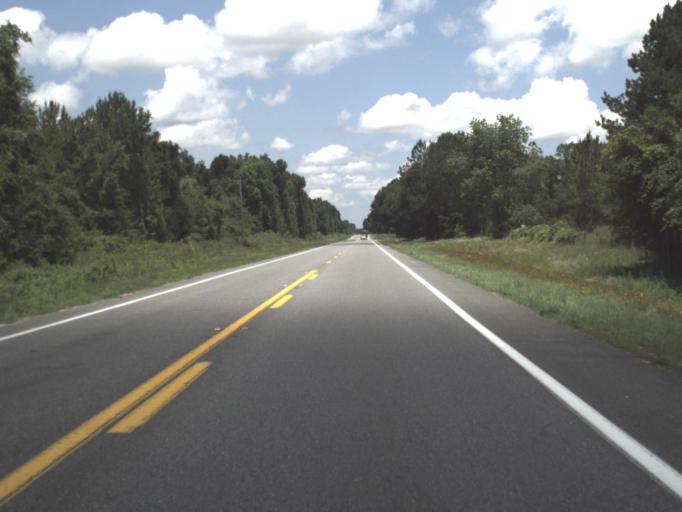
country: US
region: Florida
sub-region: Alachua County
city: High Springs
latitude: 29.8770
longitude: -82.6595
